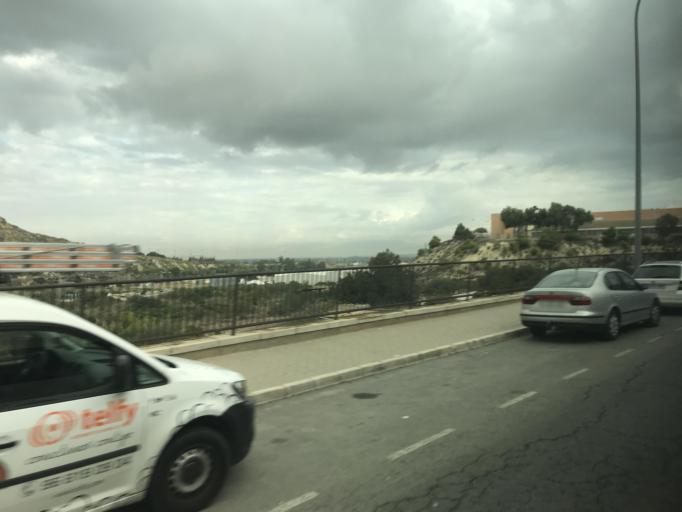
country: ES
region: Valencia
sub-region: Provincia de Alicante
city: Guardamar del Segura
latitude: 38.0844
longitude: -0.6555
